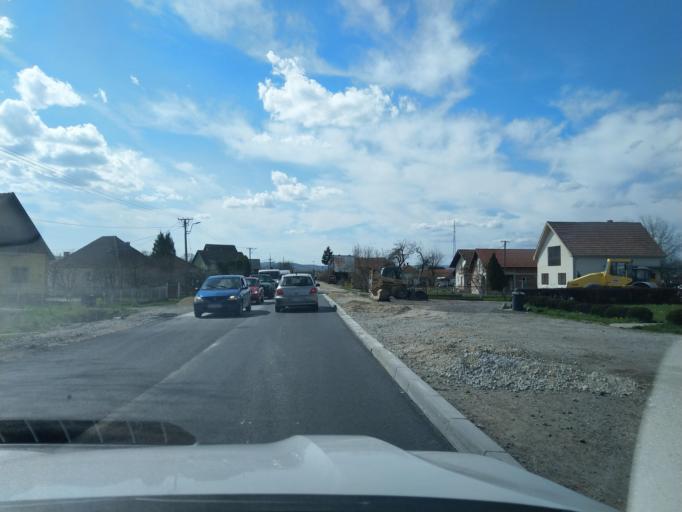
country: RS
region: Central Serbia
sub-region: Zlatiborski Okrug
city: Pozega
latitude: 43.8312
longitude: 20.0525
